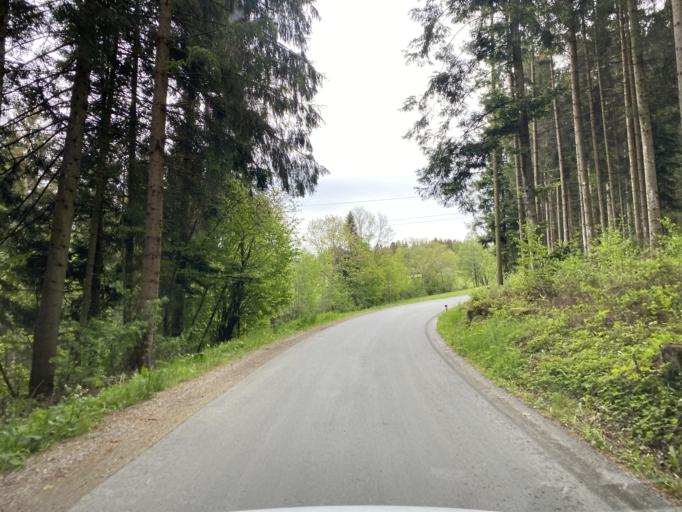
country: AT
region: Styria
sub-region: Politischer Bezirk Weiz
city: Birkfeld
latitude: 47.3354
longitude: 15.7061
